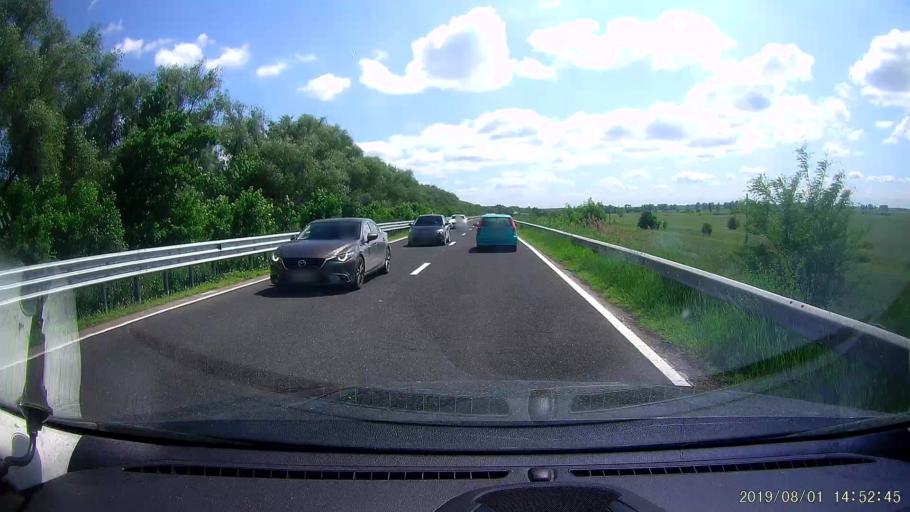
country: RO
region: Braila
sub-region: Comuna Vadeni
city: Vadeni
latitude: 45.3492
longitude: 28.0088
